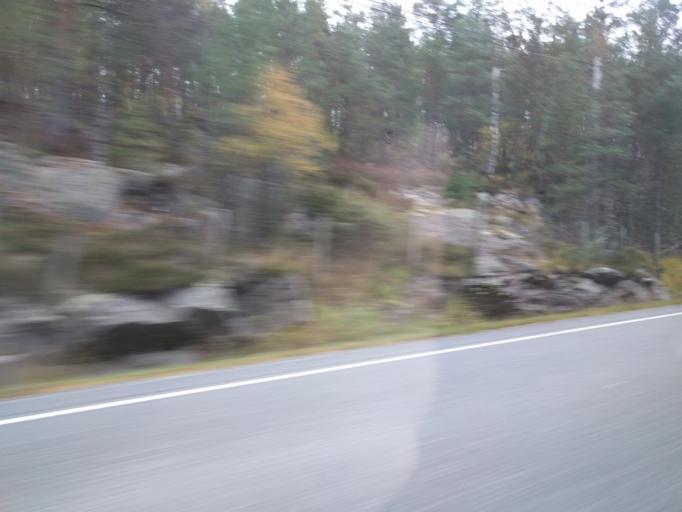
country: NO
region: Aust-Agder
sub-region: Evje og Hornnes
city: Evje
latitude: 58.4857
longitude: 7.7831
